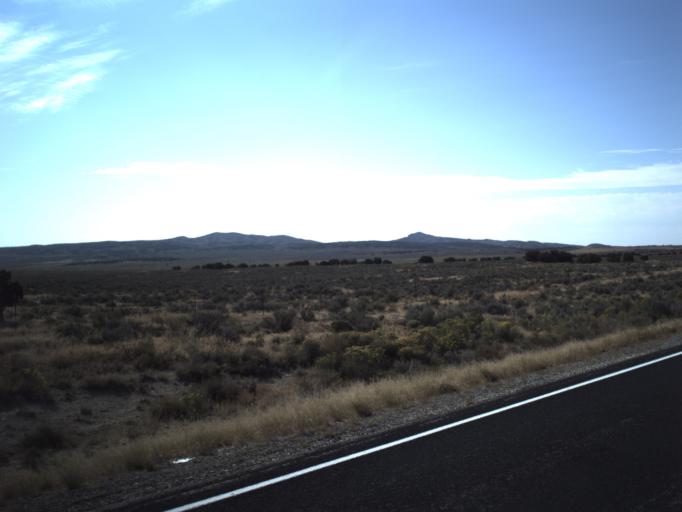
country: US
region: Idaho
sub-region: Cassia County
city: Burley
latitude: 41.7204
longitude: -113.5266
